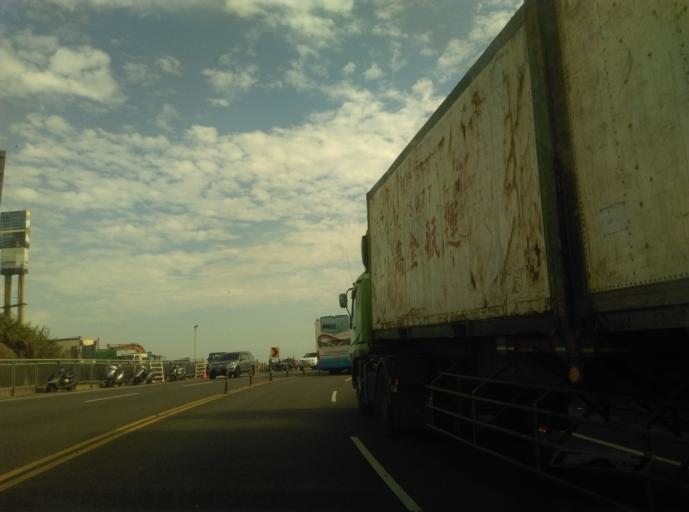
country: TW
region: Taiwan
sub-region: Keelung
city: Keelung
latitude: 25.1748
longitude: 121.7076
